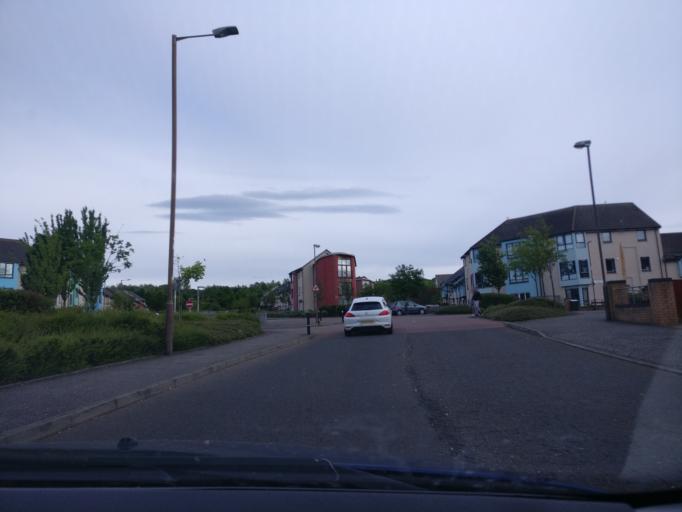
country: GB
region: Scotland
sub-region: West Lothian
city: Seafield
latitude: 55.9319
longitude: -3.1408
